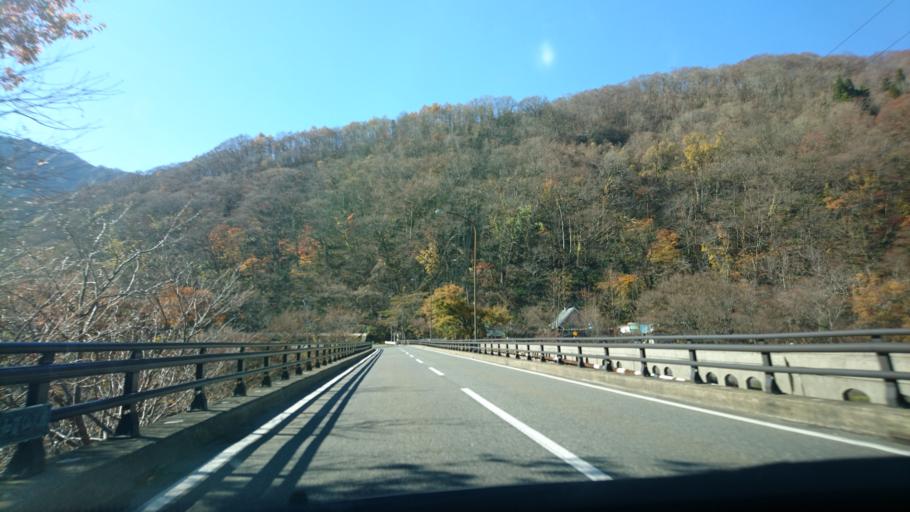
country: JP
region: Iwate
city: Kitakami
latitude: 39.3045
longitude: 140.9017
